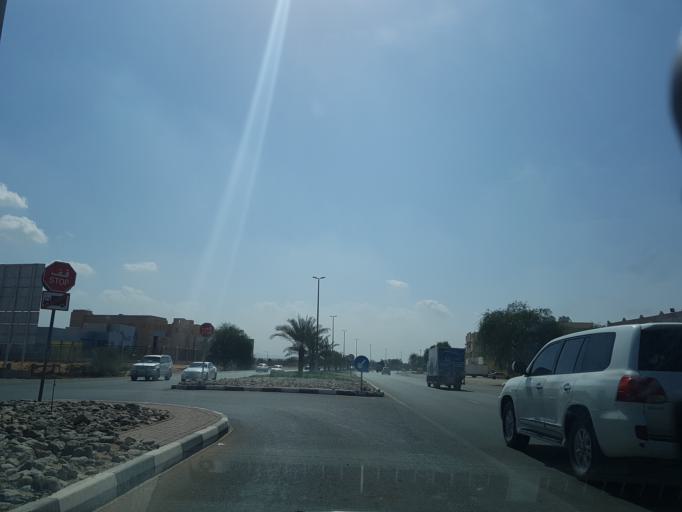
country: AE
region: Ra's al Khaymah
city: Ras al-Khaimah
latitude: 25.6950
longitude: 55.9675
